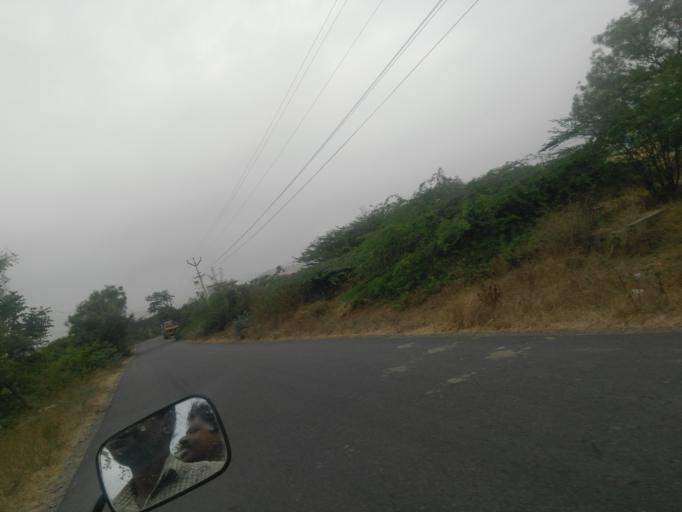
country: IN
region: Tamil Nadu
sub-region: Coimbatore
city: Karamadai
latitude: 11.2604
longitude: 76.9470
